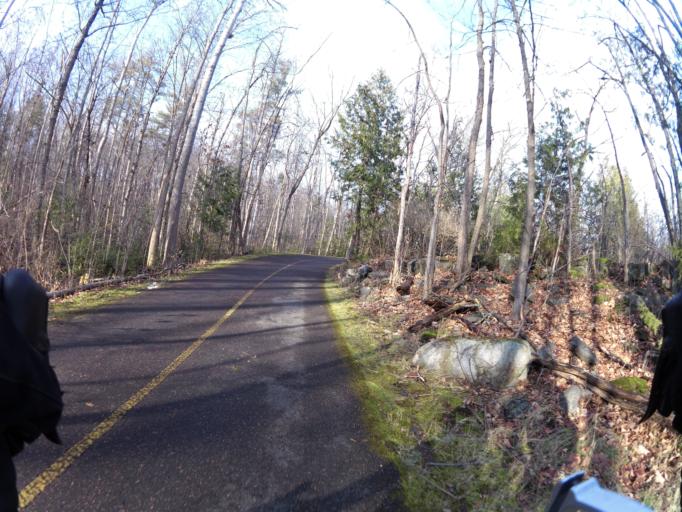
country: CA
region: Ontario
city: Ottawa
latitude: 45.4277
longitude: -75.7456
